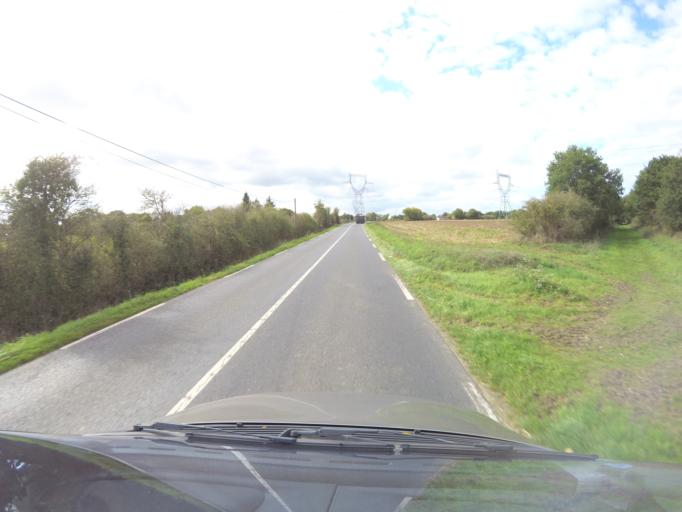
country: FR
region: Pays de la Loire
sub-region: Departement de la Loire-Atlantique
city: Fay-de-Bretagne
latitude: 47.4084
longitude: -1.7552
